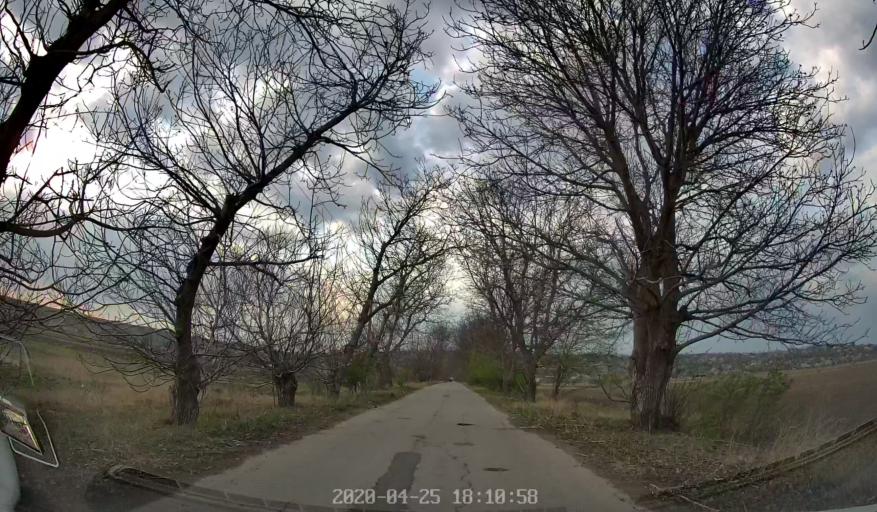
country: MD
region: Chisinau
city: Vadul lui Voda
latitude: 47.1371
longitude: 29.0728
